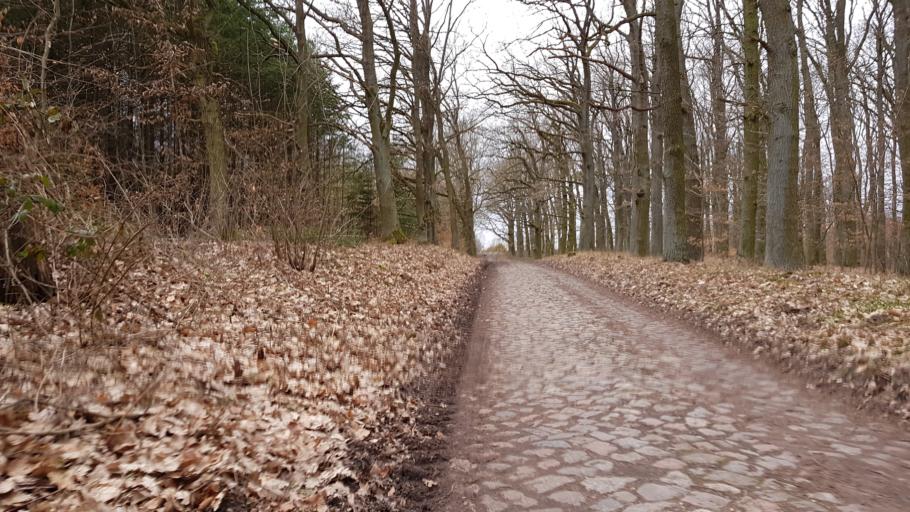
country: PL
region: West Pomeranian Voivodeship
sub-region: Powiat gryfinski
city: Banie
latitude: 53.0916
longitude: 14.7127
